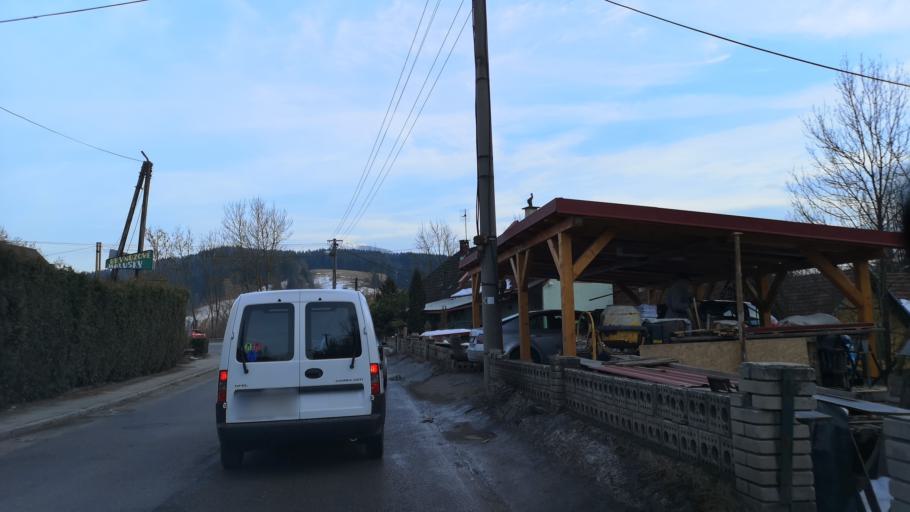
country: SK
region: Zilinsky
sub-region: Okres Dolny Kubin
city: Dolny Kubin
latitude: 49.2126
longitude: 19.2717
